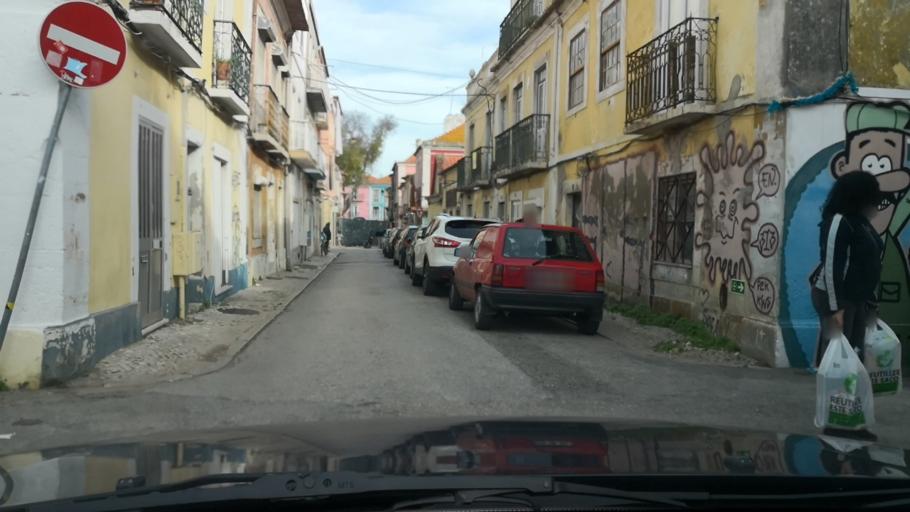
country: PT
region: Setubal
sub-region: Setubal
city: Setubal
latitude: 38.5231
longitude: -8.9003
